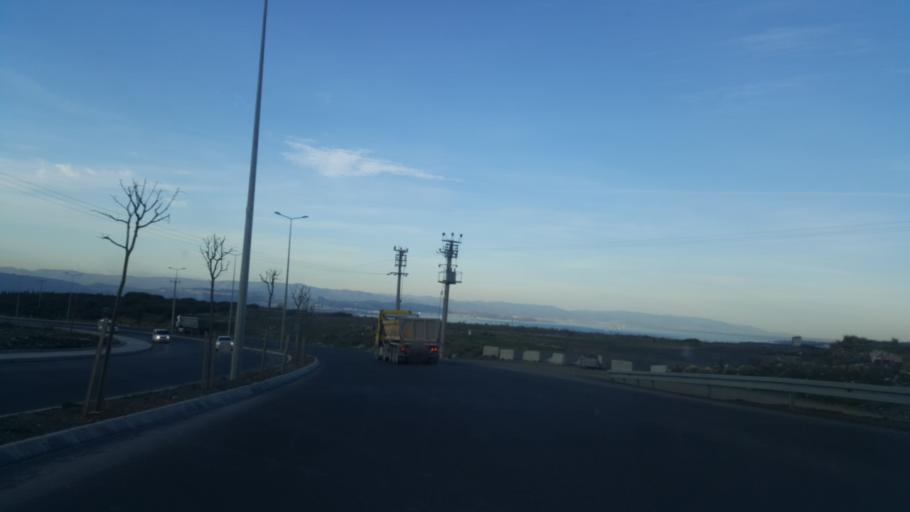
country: TR
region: Kocaeli
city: Tavsancil
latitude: 40.8047
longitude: 29.5521
